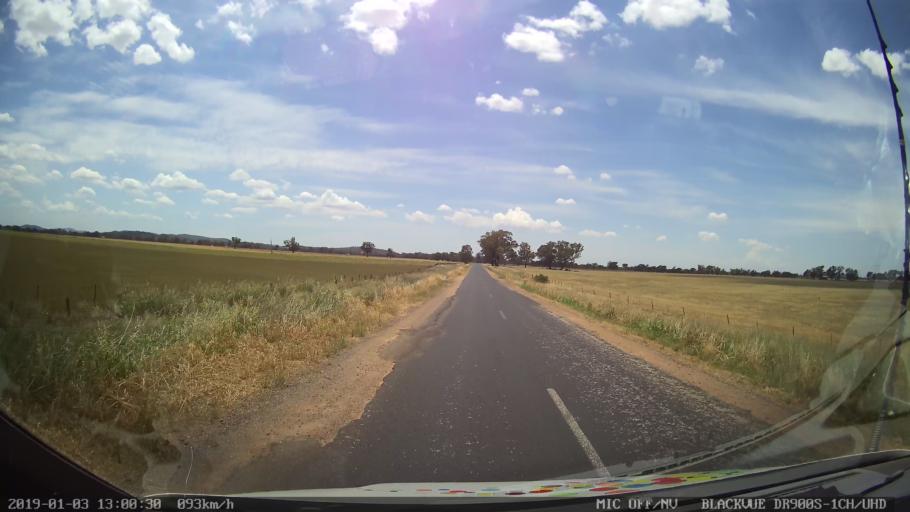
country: AU
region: New South Wales
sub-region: Cabonne
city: Canowindra
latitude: -33.6306
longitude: 148.4046
